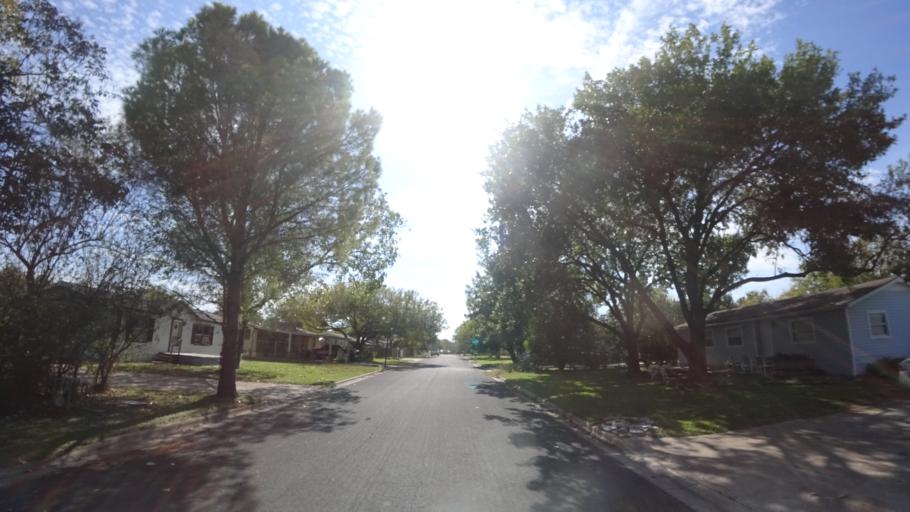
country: US
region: Texas
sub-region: Travis County
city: Pflugerville
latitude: 30.4109
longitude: -97.6290
